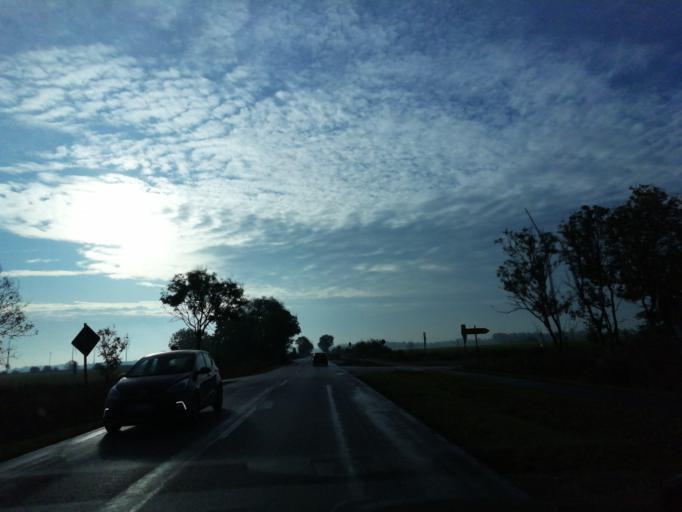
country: DE
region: Lower Saxony
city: Fedderwarden
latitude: 53.6116
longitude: 8.0415
